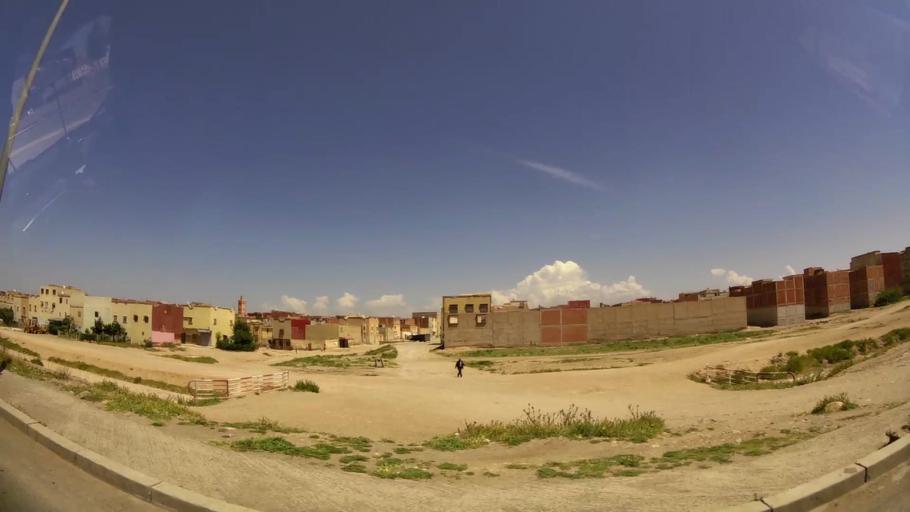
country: MA
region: Oriental
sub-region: Oujda-Angad
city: Oujda
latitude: 34.6907
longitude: -1.9433
